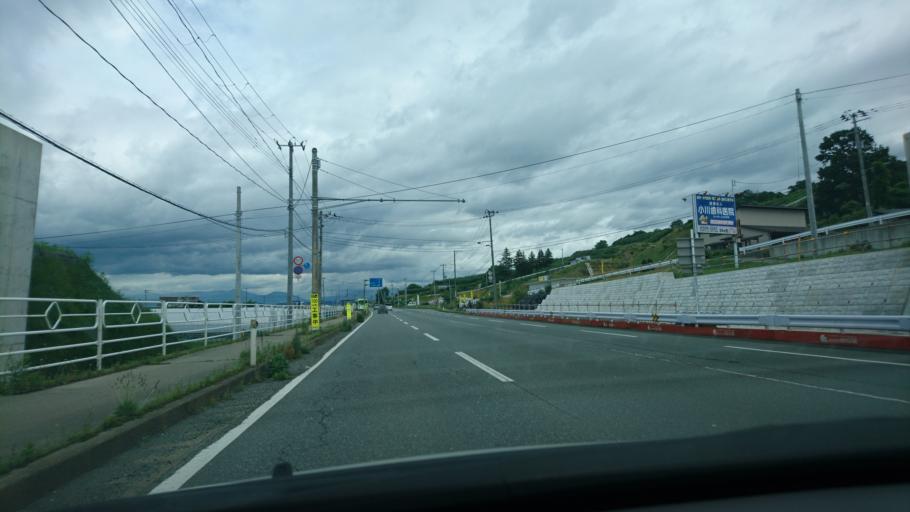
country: JP
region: Iwate
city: Morioka-shi
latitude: 39.6596
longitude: 141.1791
